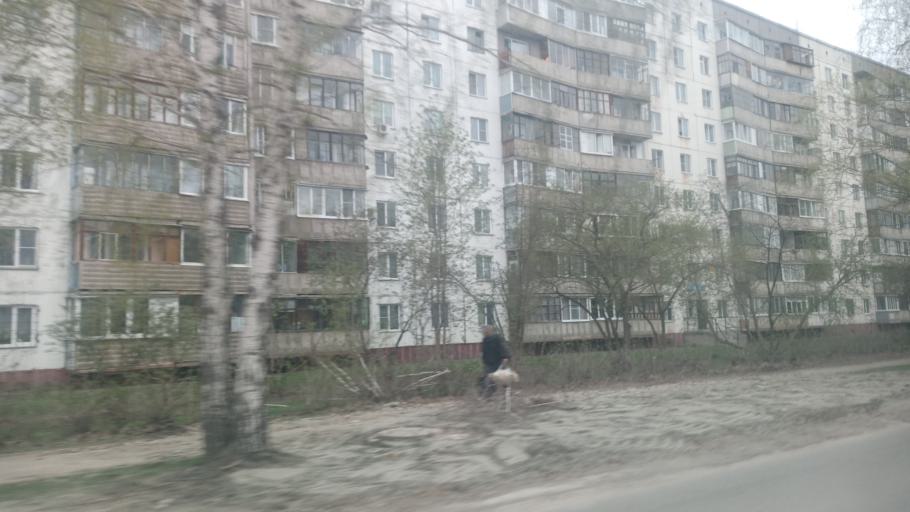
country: RU
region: Altai Krai
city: Yuzhnyy
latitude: 53.2498
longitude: 83.6887
